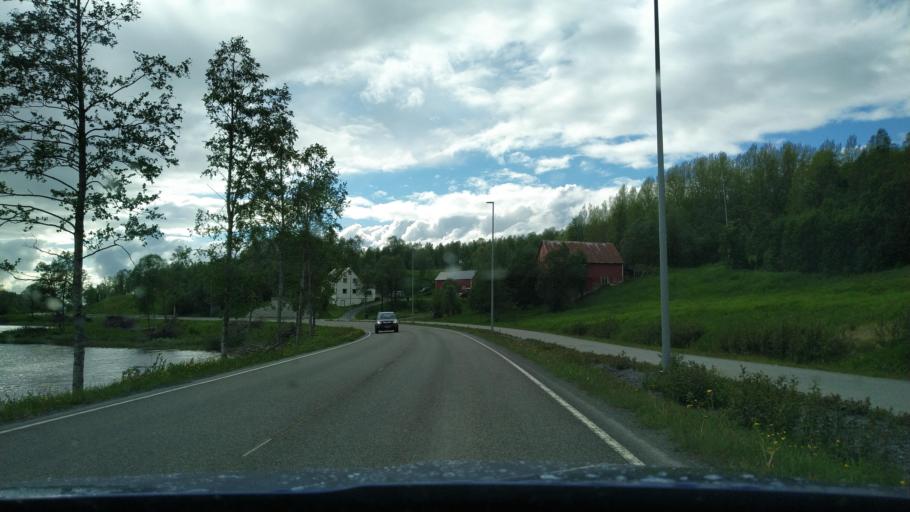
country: NO
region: Troms
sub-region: Sorreisa
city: Sorreisa
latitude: 69.1743
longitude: 18.1034
